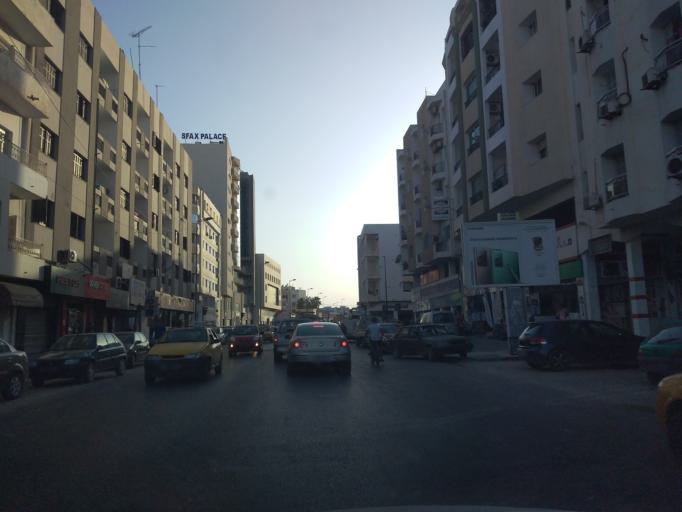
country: TN
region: Safaqis
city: Sfax
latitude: 34.7455
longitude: 10.7633
